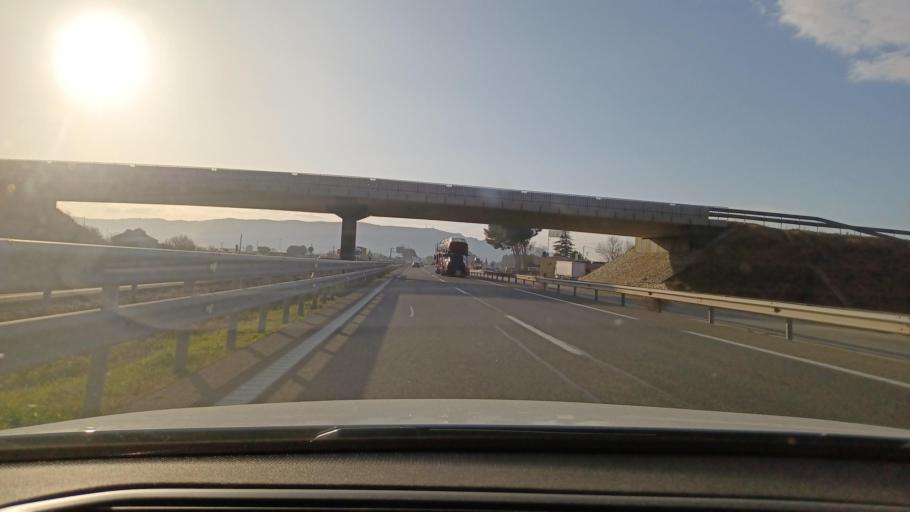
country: ES
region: Valencia
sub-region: Provincia de Alicante
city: Villena
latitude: 38.6730
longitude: -0.8891
